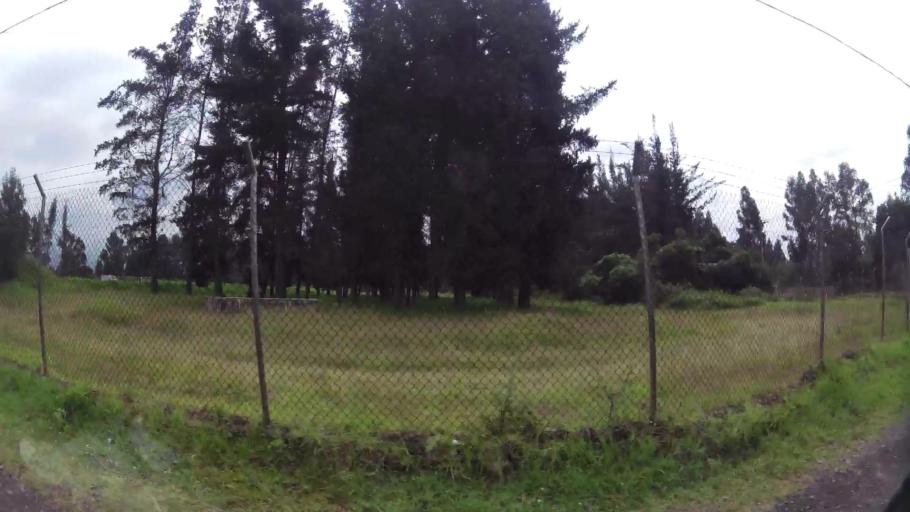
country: EC
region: Pichincha
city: Sangolqui
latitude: -0.3497
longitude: -78.4732
